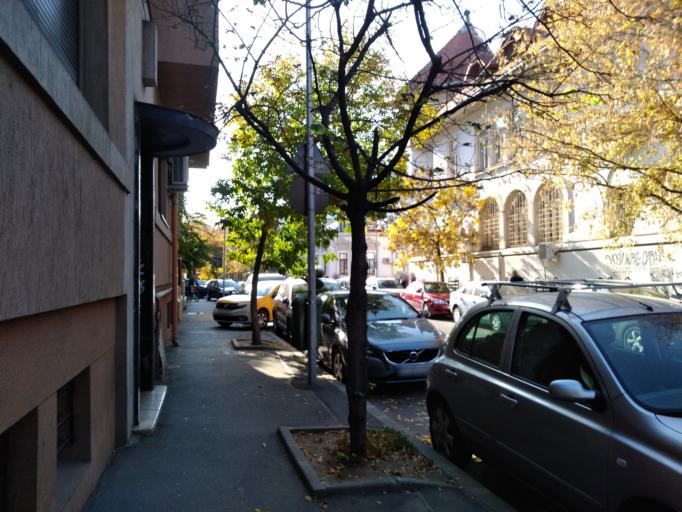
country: RO
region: Bucuresti
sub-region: Municipiul Bucuresti
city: Bucuresti
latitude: 44.4412
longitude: 26.0859
